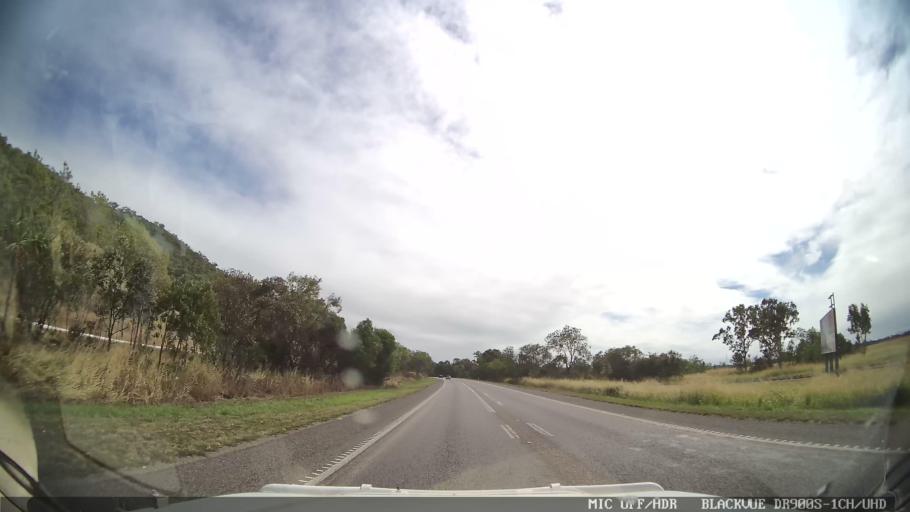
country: AU
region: Queensland
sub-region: Hinchinbrook
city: Ingham
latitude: -19.0125
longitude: 146.3646
